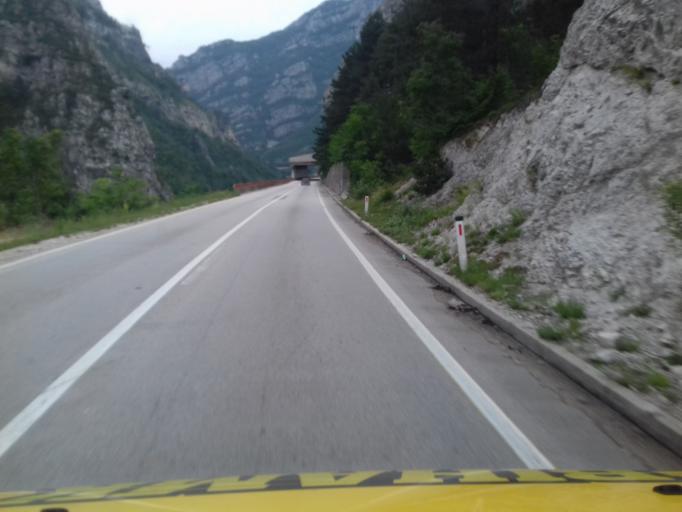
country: BA
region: Federation of Bosnia and Herzegovina
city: Jablanica
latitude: 43.6232
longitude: 17.7499
